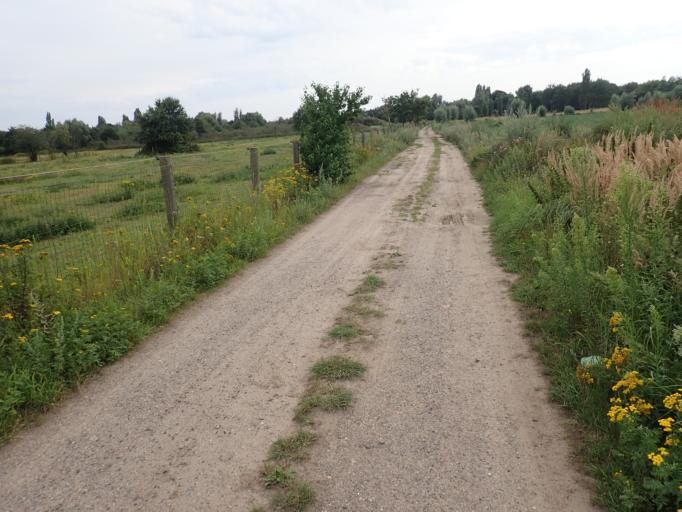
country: BE
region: Flanders
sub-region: Provincie Antwerpen
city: Ranst
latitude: 51.2127
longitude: 4.5592
